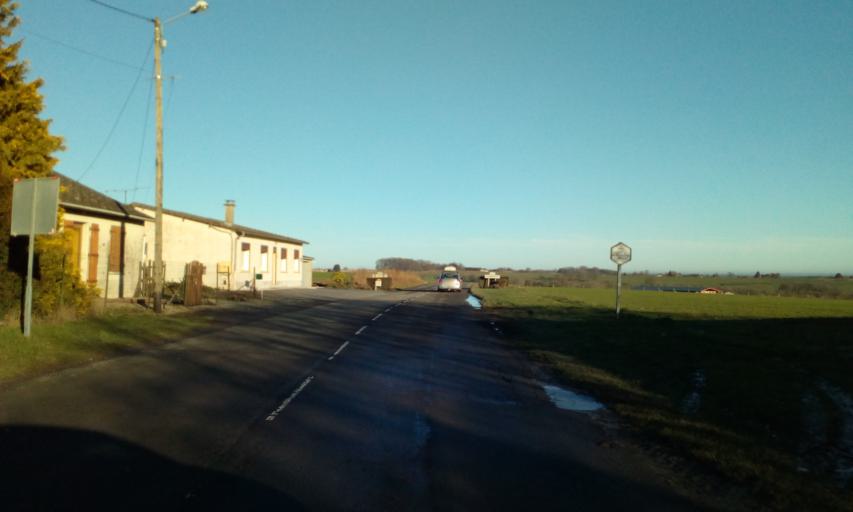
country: FR
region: Picardie
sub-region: Departement de l'Aisne
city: Rozoy-sur-Serre
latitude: 49.7095
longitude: 4.2254
